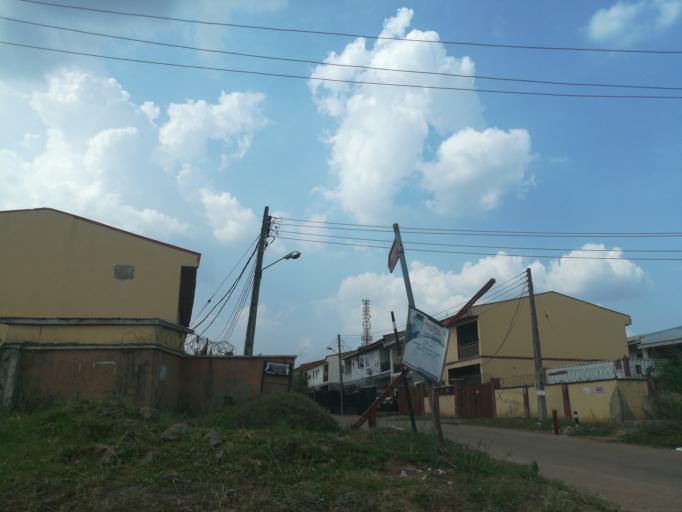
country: NG
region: Abuja Federal Capital Territory
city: Abuja
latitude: 9.0775
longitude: 7.4129
